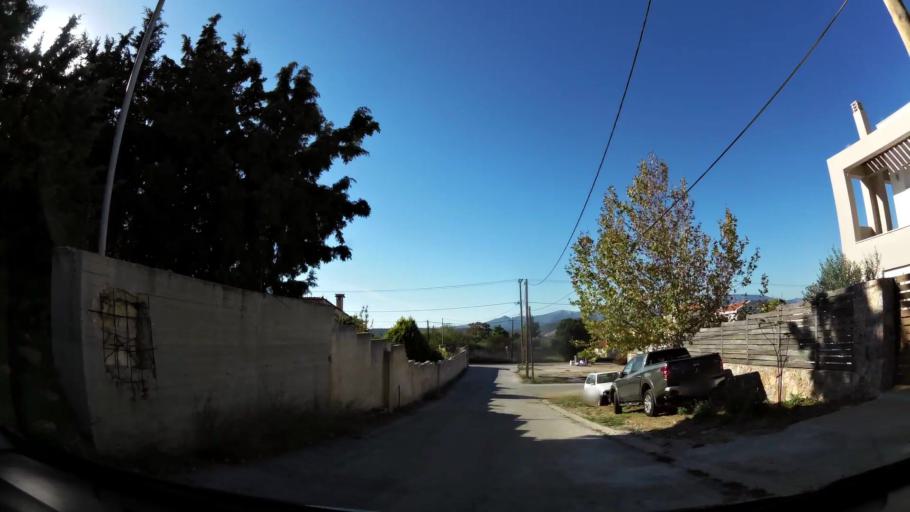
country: GR
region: Attica
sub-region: Nomarchia Anatolikis Attikis
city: Kalyvia Thorikou
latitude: 37.8323
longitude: 23.9293
